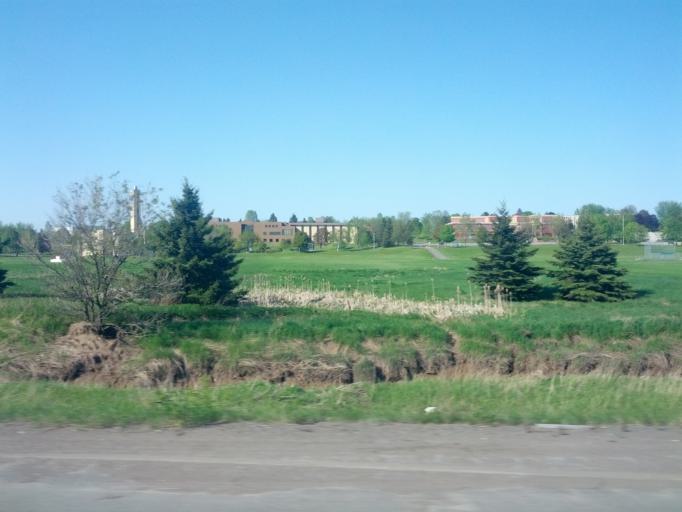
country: CA
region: New Brunswick
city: Moncton
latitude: 46.1022
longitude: -64.7896
